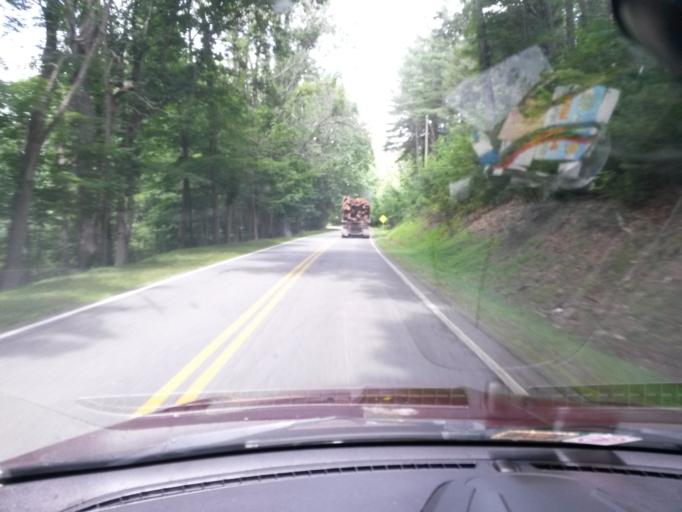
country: US
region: Virginia
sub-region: City of Covington
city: Covington
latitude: 37.7567
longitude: -80.1301
